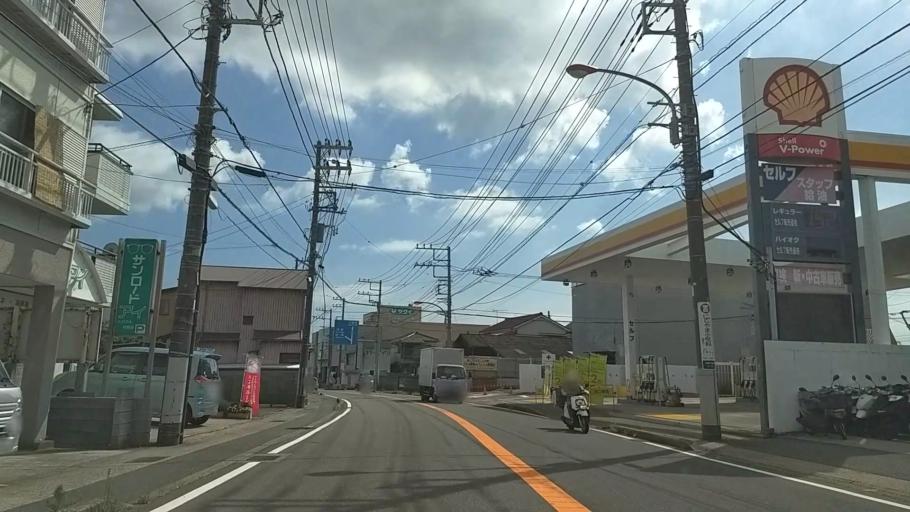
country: JP
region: Kanagawa
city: Miura
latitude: 35.1513
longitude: 139.6290
